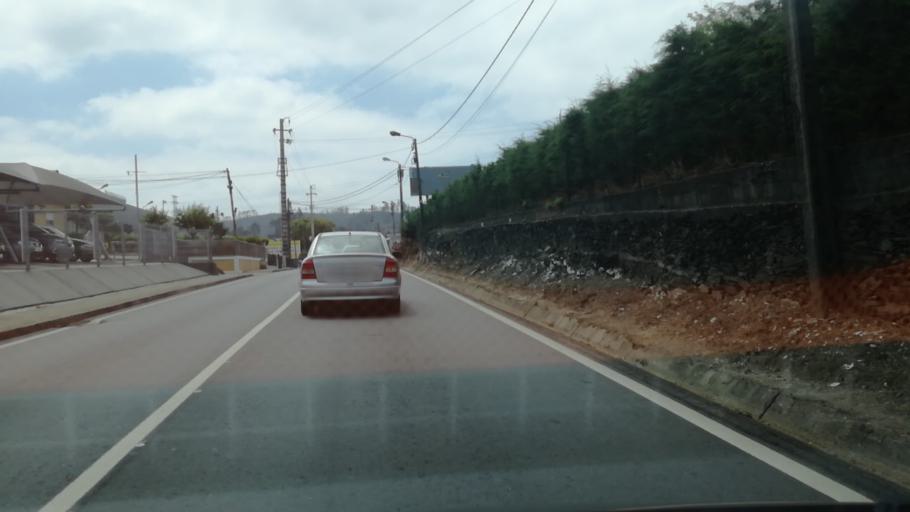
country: PT
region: Porto
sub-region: Trofa
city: Sao Romao do Coronado
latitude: 41.3137
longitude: -8.5808
